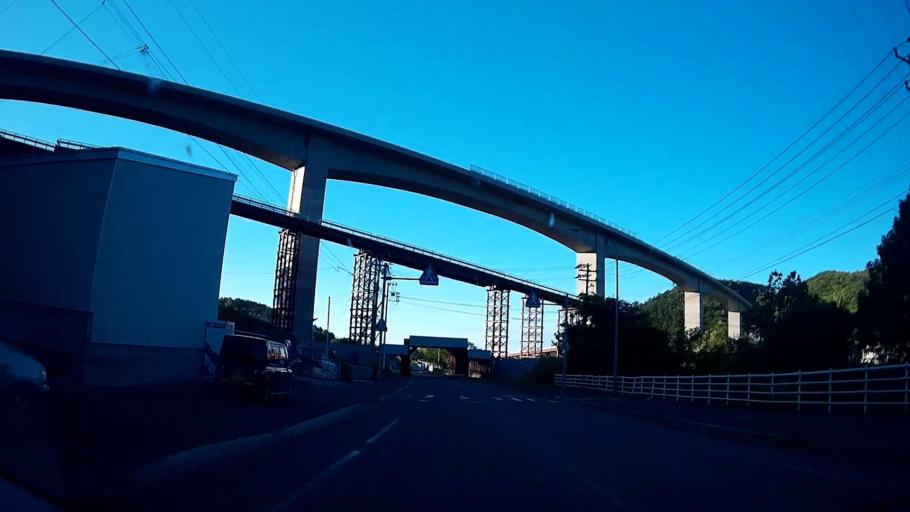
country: JP
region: Hokkaido
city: Otaru
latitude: 43.1517
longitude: 141.0412
